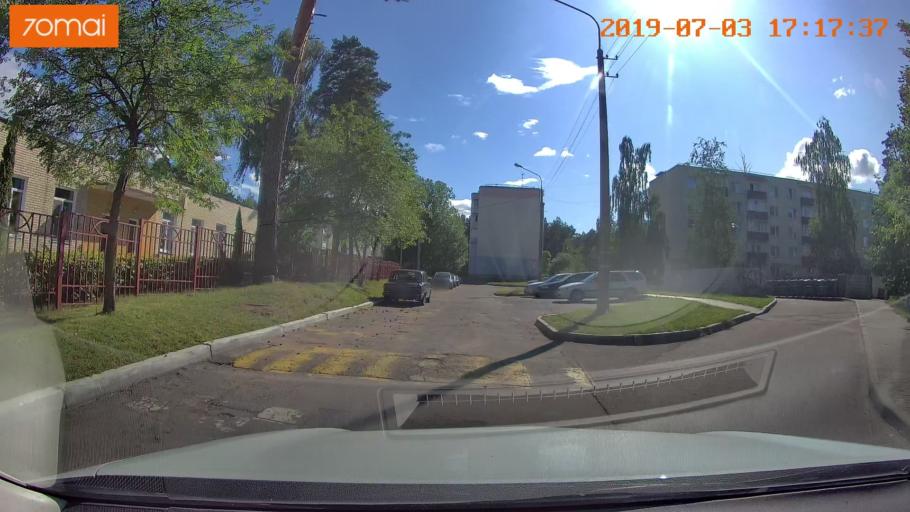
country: BY
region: Minsk
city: Vyaliki Trastsyanets
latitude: 53.9088
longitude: 27.6714
